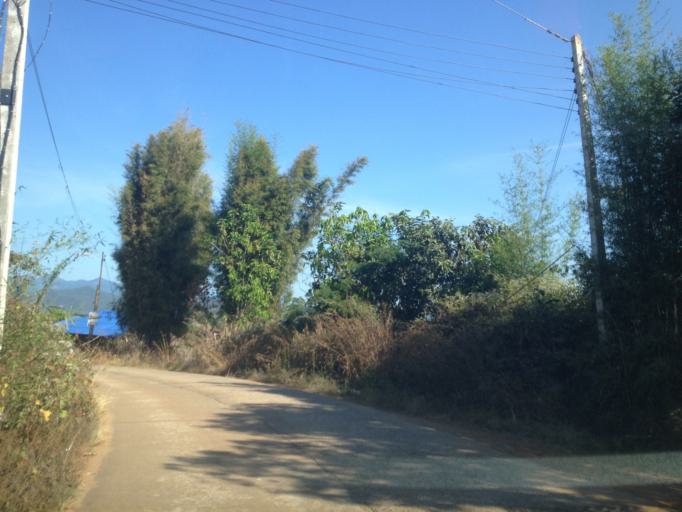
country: TH
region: Mae Hong Son
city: Ban Huai I Huak
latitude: 18.0435
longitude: 98.1656
